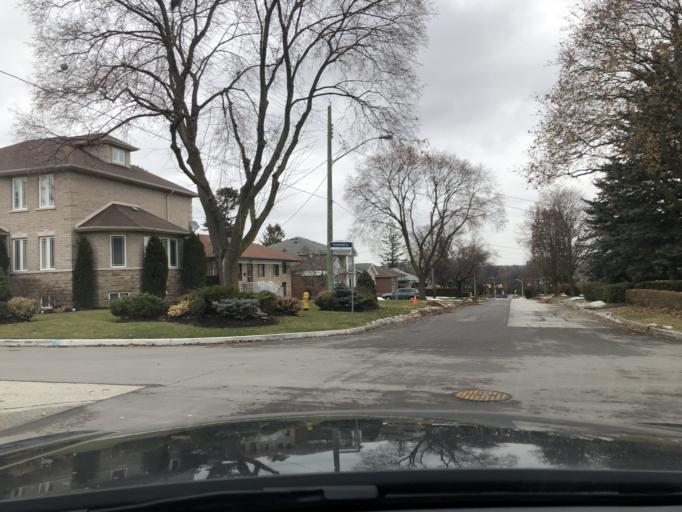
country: CA
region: Ontario
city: Etobicoke
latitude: 43.6920
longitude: -79.5202
